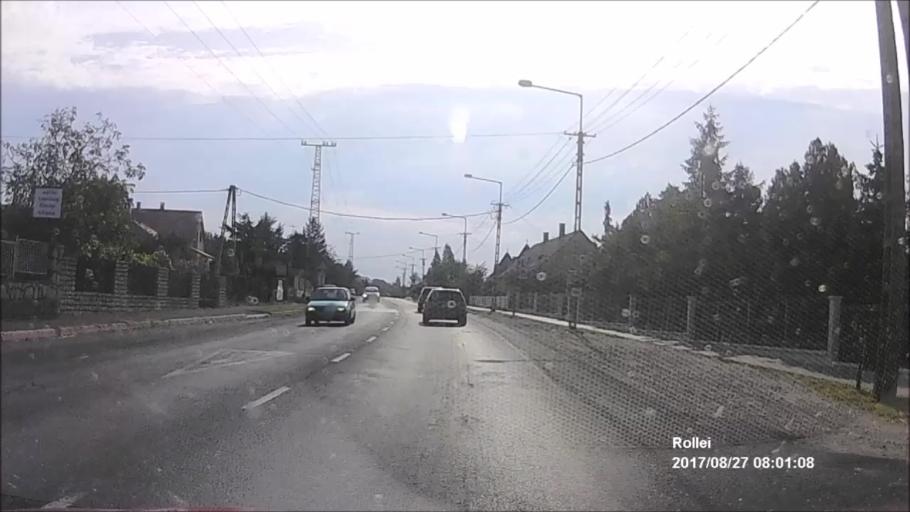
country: HU
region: Zala
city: Vonyarcvashegy
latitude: 46.7631
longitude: 17.3088
